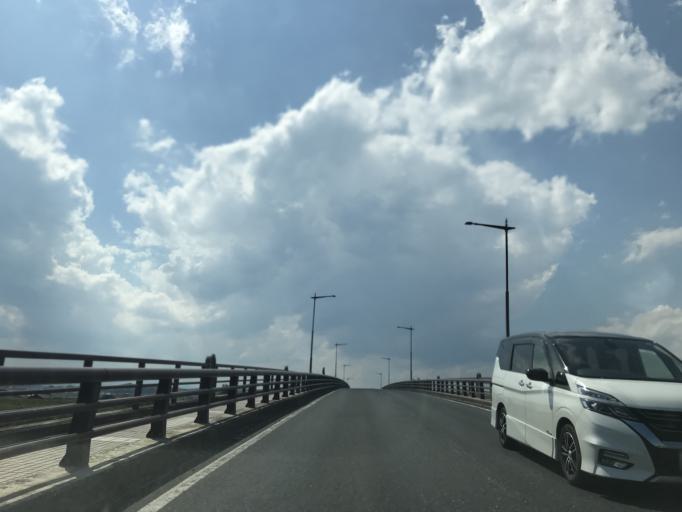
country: JP
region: Miyagi
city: Wakuya
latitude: 38.4720
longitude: 141.1276
